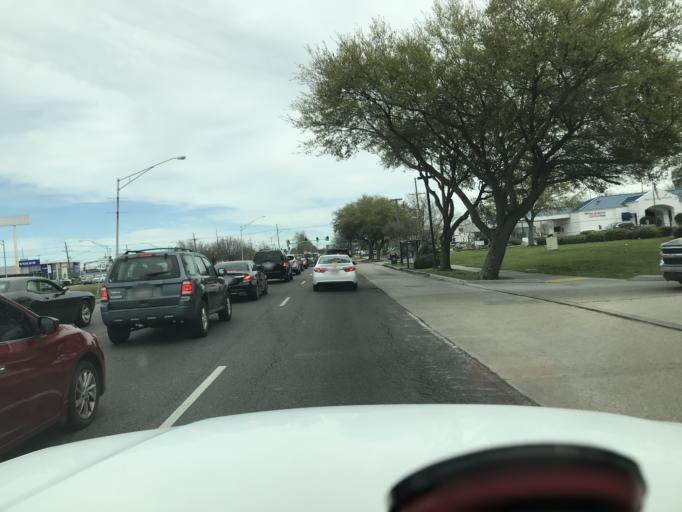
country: US
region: Louisiana
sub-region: Jefferson Parish
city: Metairie
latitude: 30.0035
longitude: -90.1638
